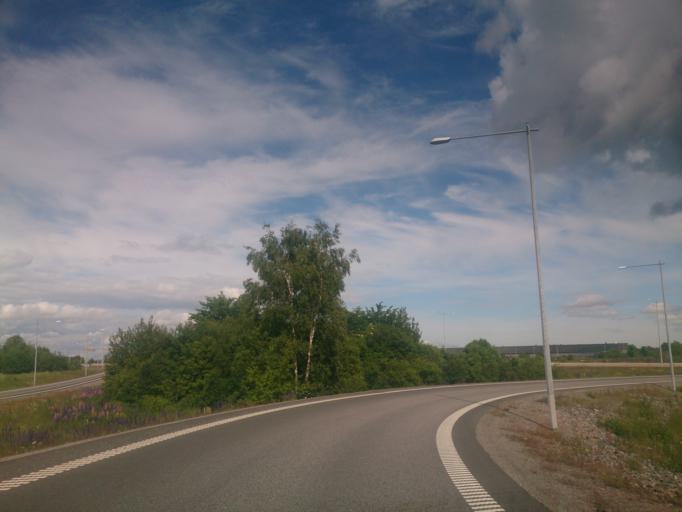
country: SE
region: OEstergoetland
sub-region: Norrkopings Kommun
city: Norrkoping
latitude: 58.6291
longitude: 16.1504
